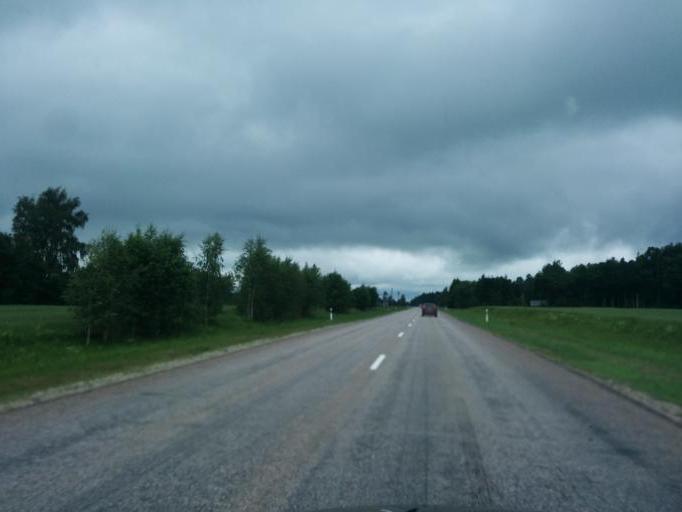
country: LV
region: Beverina
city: Murmuiza
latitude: 57.4841
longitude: 25.6028
